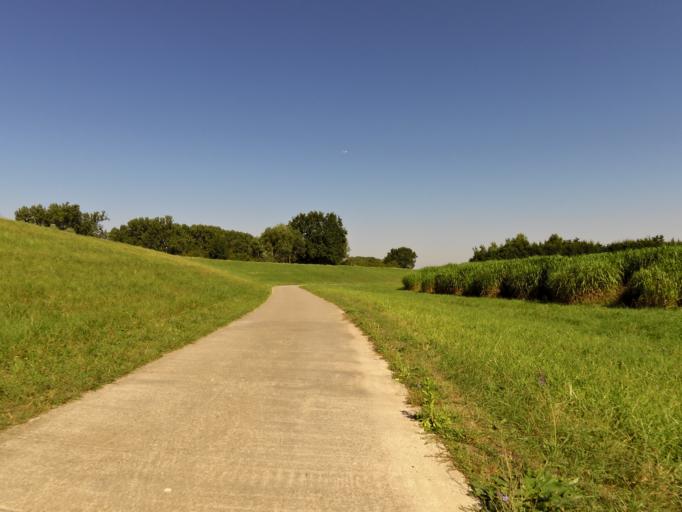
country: DE
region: Rheinland-Pfalz
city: Oppenheim
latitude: 49.8418
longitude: 8.4049
